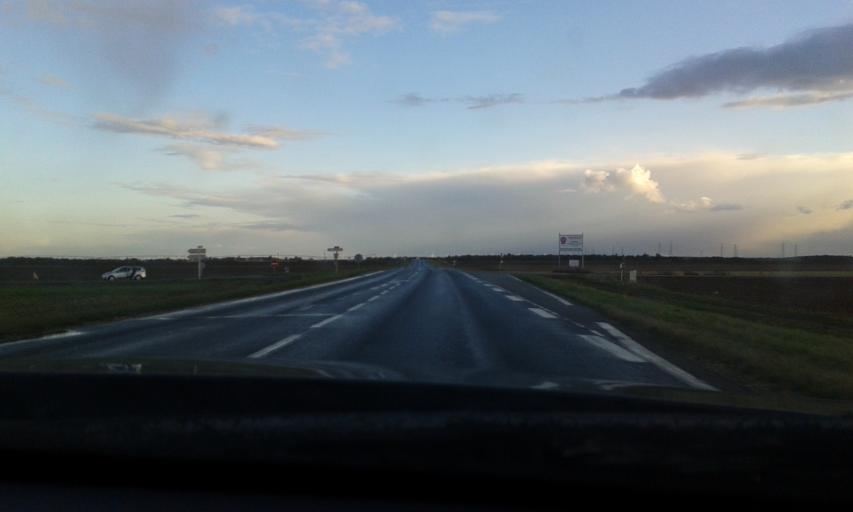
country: FR
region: Centre
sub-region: Departement d'Eure-et-Loir
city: Janville
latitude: 48.2389
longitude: 1.7819
